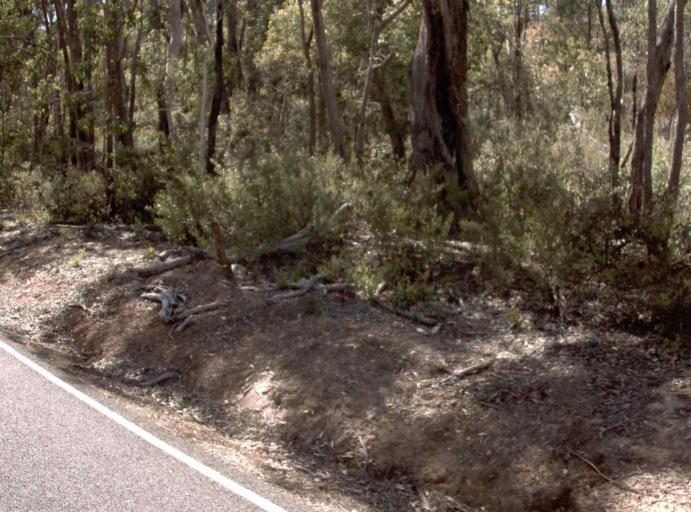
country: AU
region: New South Wales
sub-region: Bombala
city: Bombala
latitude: -37.1367
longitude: 148.7375
